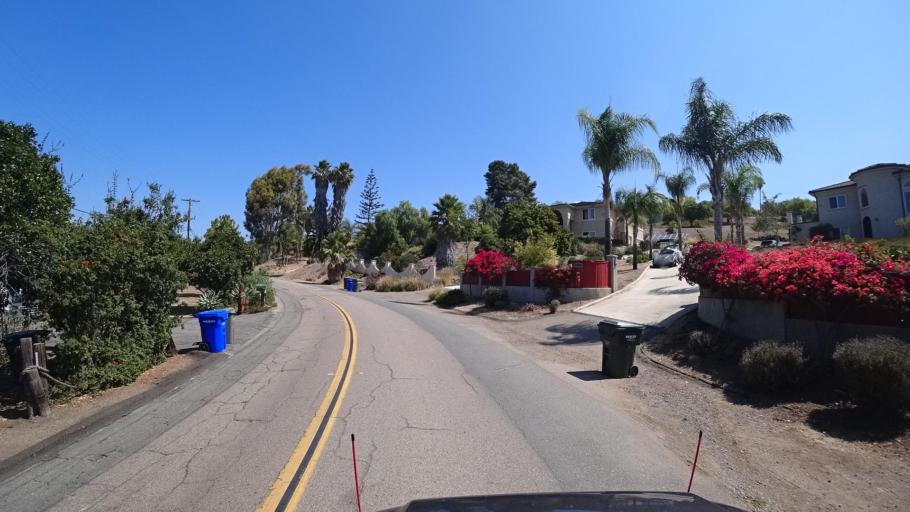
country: US
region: California
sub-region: San Diego County
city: San Marcos
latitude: 33.1706
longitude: -117.2004
